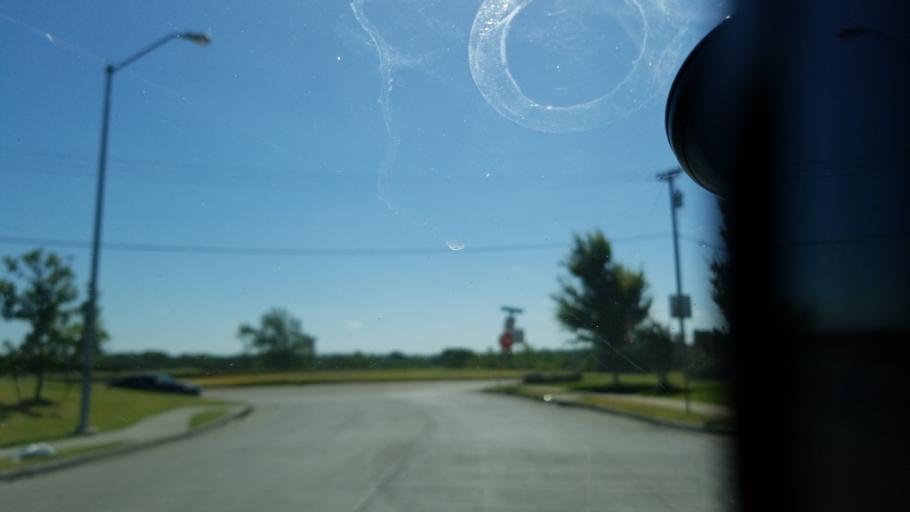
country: US
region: Texas
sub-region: Dallas County
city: Cockrell Hill
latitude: 32.6858
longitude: -96.8249
